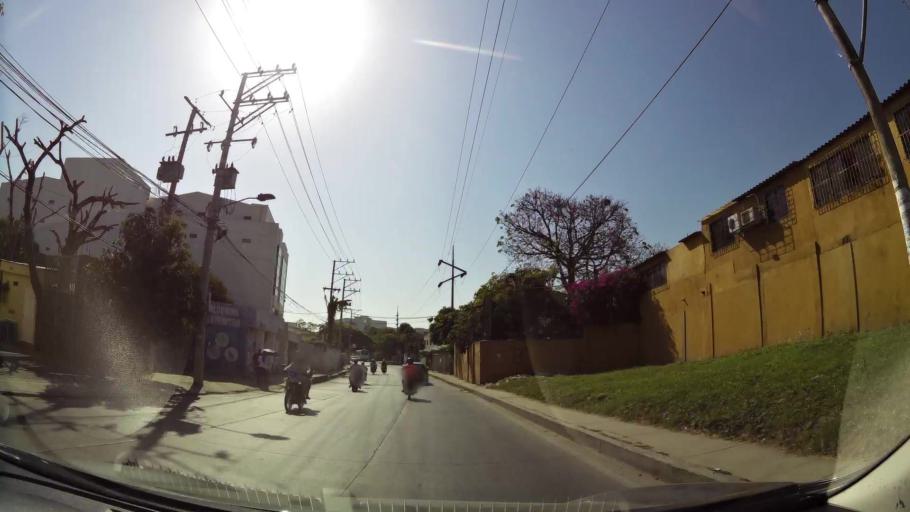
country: CO
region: Bolivar
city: Cartagena
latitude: 10.3930
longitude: -75.4755
